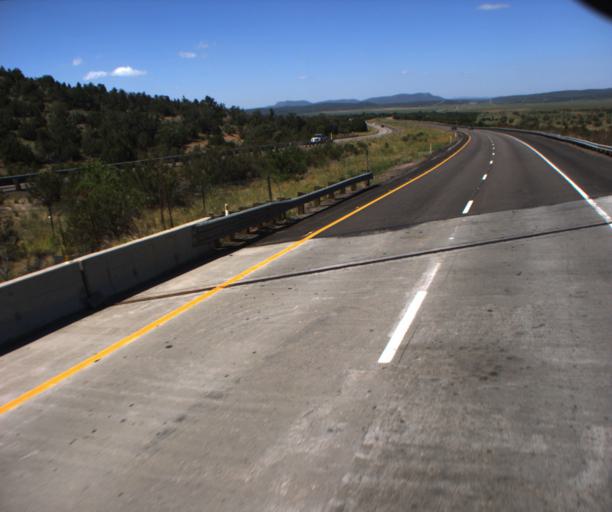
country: US
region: Arizona
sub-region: Mohave County
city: Peach Springs
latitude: 35.2855
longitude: -113.1213
